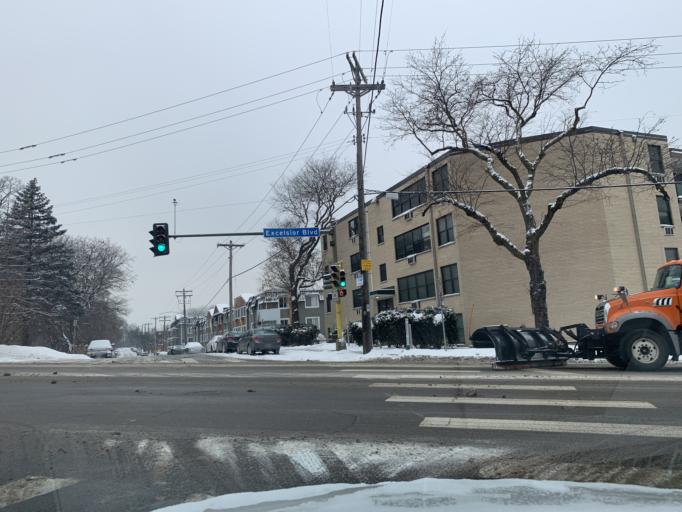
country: US
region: Minnesota
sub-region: Hennepin County
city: Saint Louis Park
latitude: 44.9450
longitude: -93.3232
